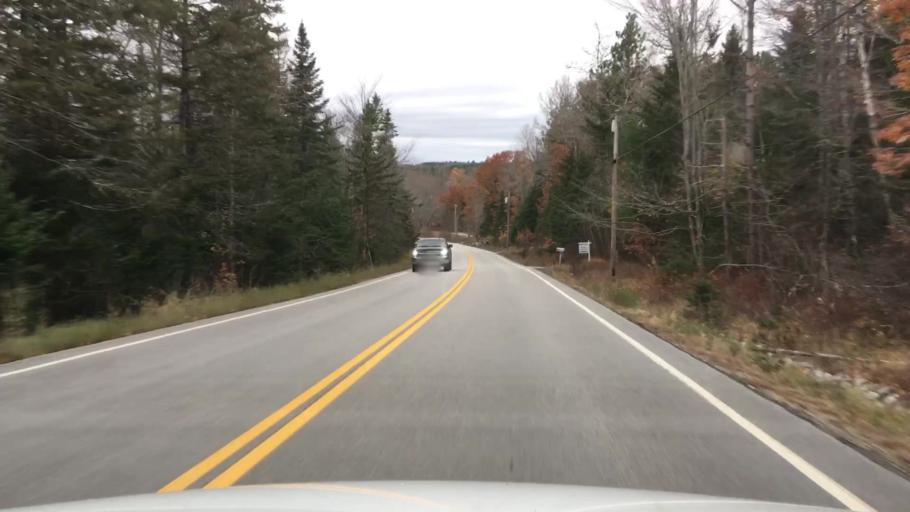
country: US
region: Maine
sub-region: Hancock County
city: Penobscot
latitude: 44.4989
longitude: -68.6486
